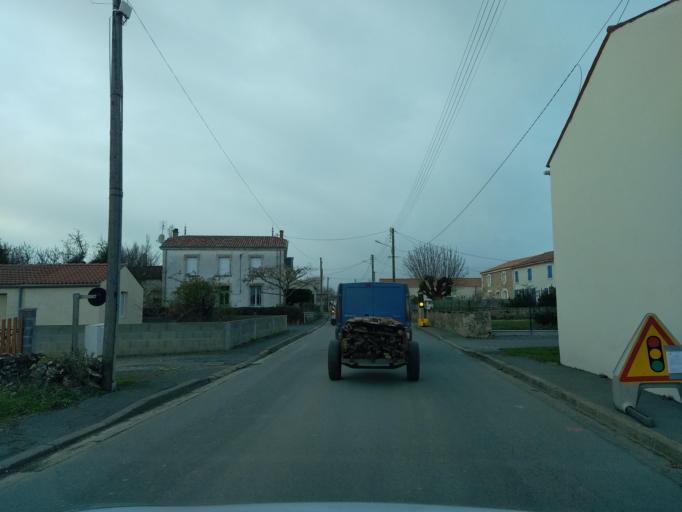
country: FR
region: Pays de la Loire
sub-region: Departement de la Vendee
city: Vix
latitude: 46.3581
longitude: -0.8507
